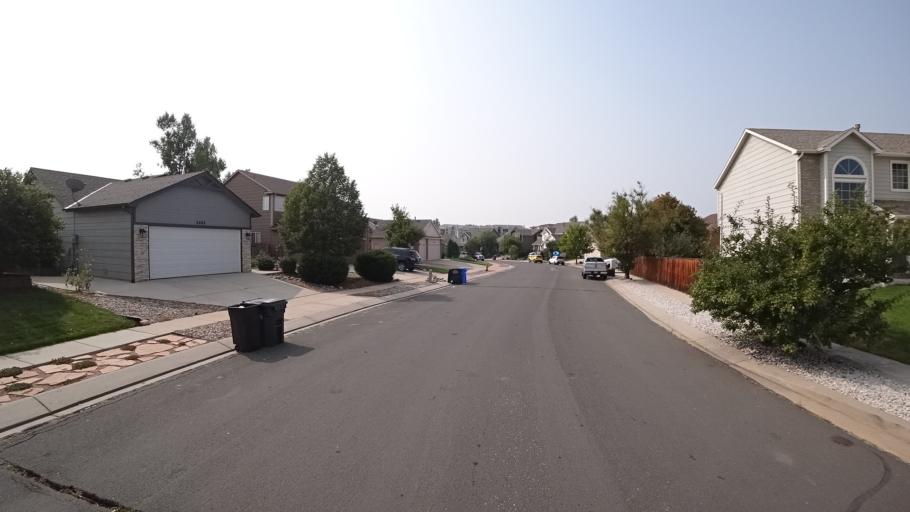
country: US
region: Colorado
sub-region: El Paso County
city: Cimarron Hills
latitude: 38.9274
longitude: -104.7369
